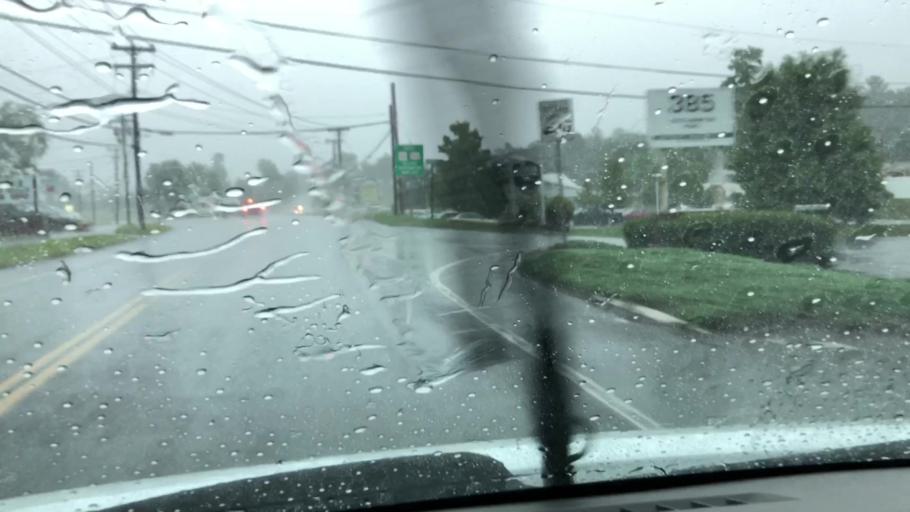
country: US
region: Massachusetts
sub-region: Hampden County
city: Westfield
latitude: 42.1520
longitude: -72.7261
